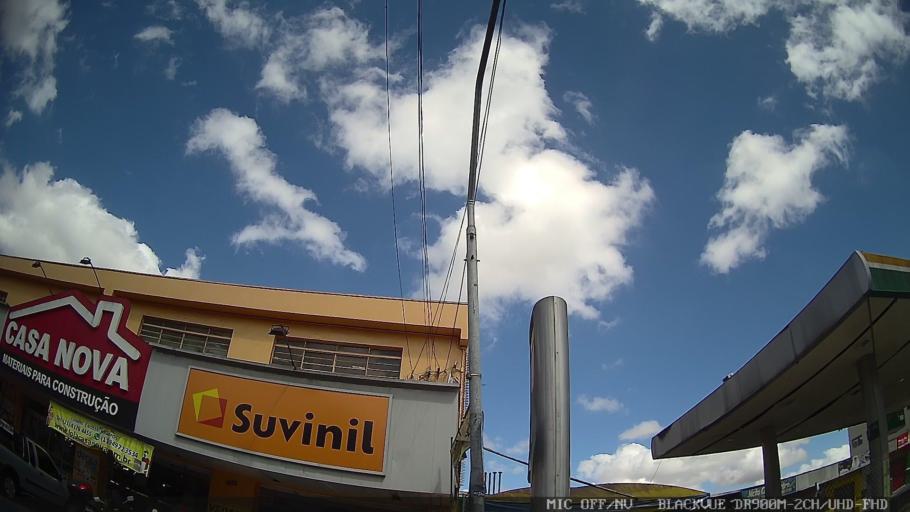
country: BR
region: Sao Paulo
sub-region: Diadema
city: Diadema
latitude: -23.6646
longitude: -46.6076
